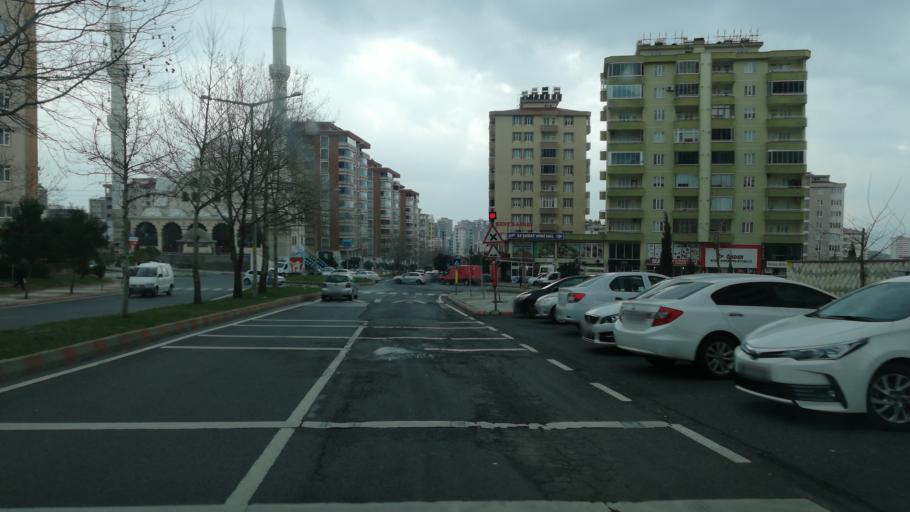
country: TR
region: Kahramanmaras
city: Kahramanmaras
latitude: 37.5875
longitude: 36.8784
